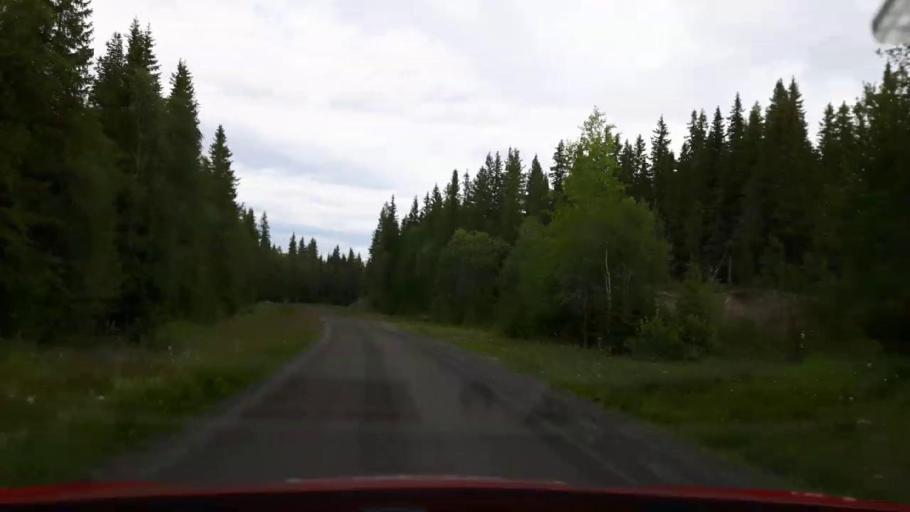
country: SE
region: Jaemtland
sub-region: OEstersunds Kommun
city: Lit
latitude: 63.4069
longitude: 15.2367
